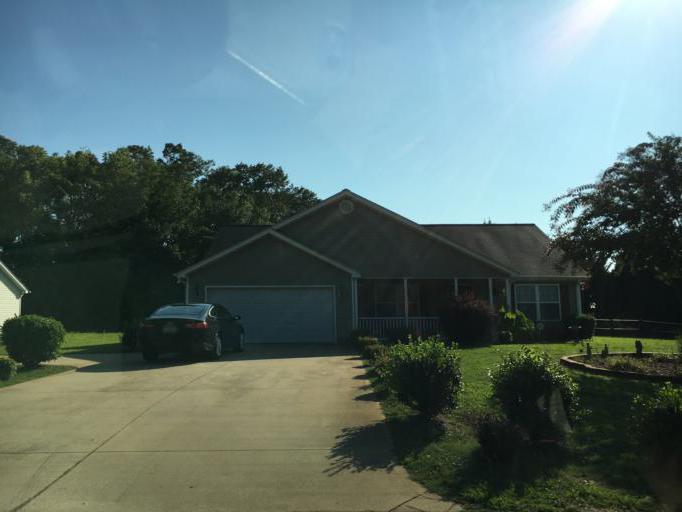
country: US
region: South Carolina
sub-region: Spartanburg County
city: Duncan
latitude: 34.8921
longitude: -82.1166
